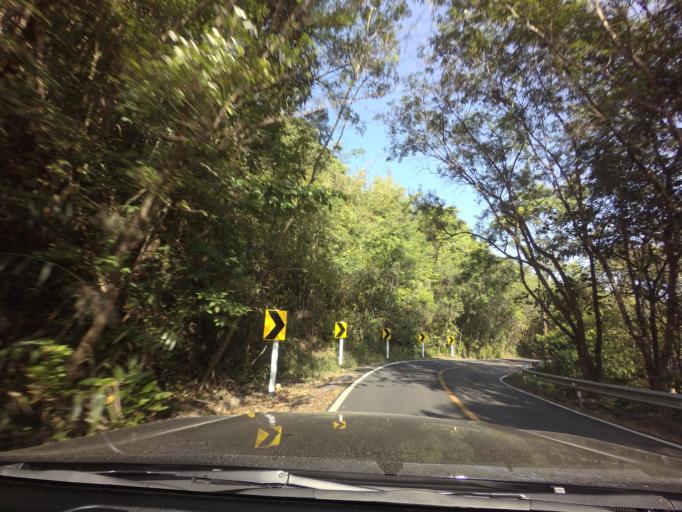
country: TH
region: Kanchanaburi
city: Thong Pha Phum
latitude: 14.6887
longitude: 98.4042
